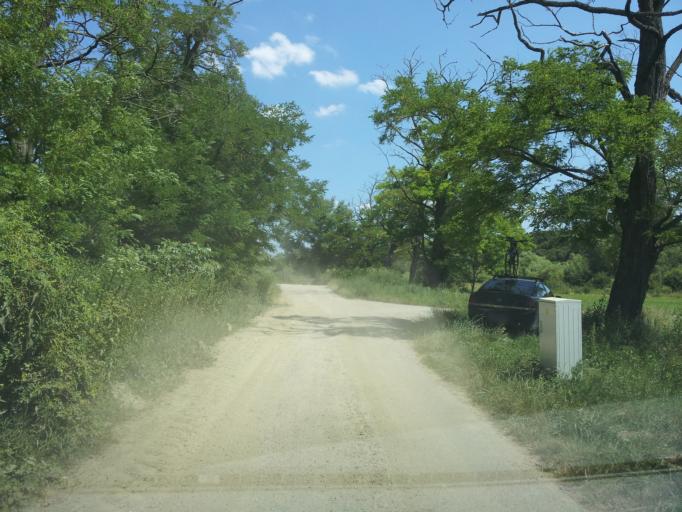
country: HU
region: Fejer
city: Many
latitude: 47.5657
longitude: 18.5984
